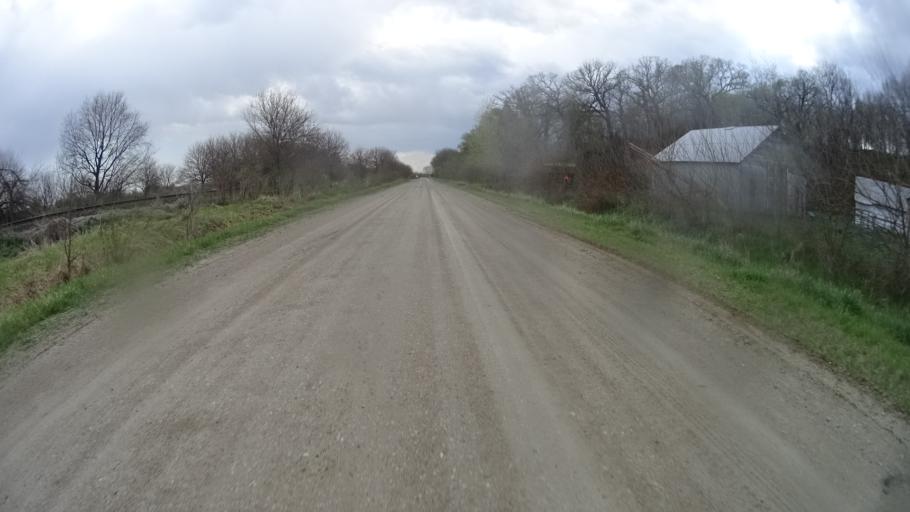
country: US
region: Nebraska
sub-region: Sarpy County
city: Offutt Air Force Base
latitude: 41.0876
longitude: -95.9156
